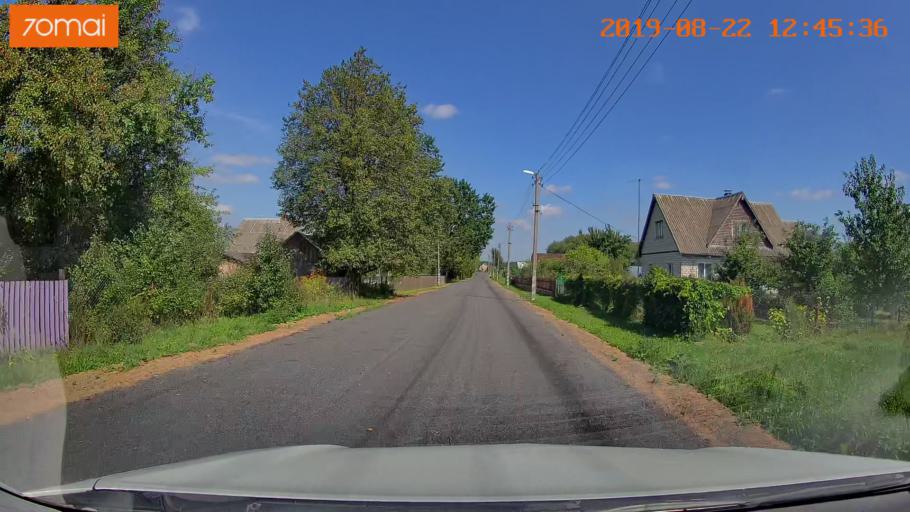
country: BY
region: Minsk
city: Prawdzinski
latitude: 53.4588
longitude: 27.6208
